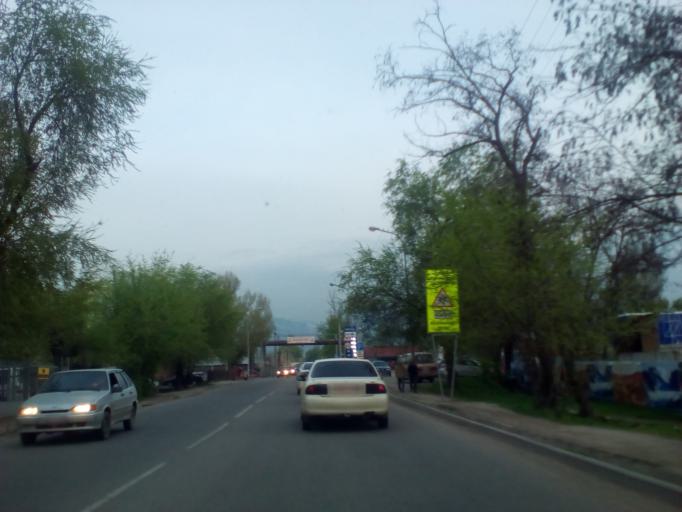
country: KZ
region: Almaty Qalasy
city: Almaty
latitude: 43.2345
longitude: 76.8251
